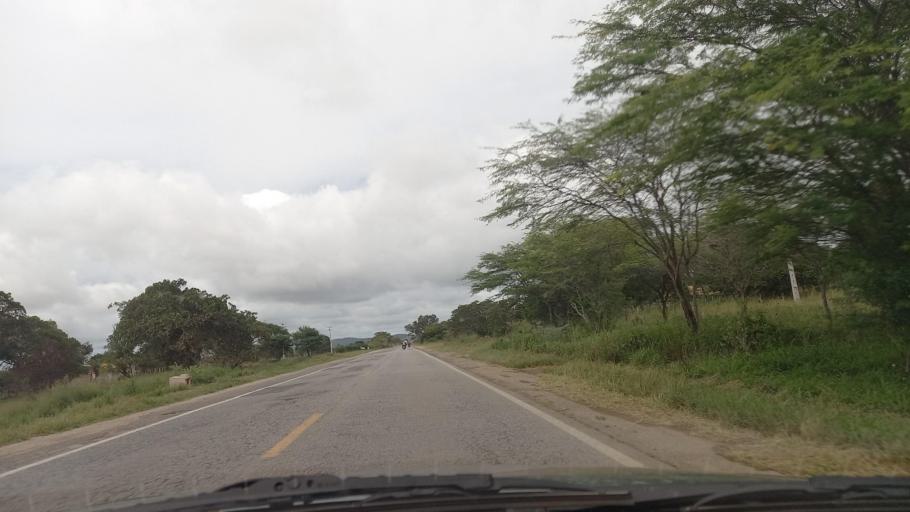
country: BR
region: Pernambuco
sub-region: Sao Joao
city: Sao Joao
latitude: -8.8799
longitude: -36.4221
